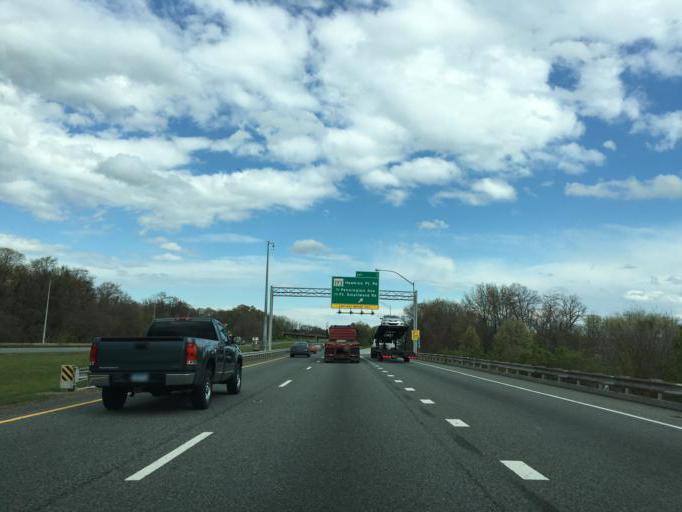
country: US
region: Maryland
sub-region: Anne Arundel County
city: Brooklyn Park
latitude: 39.2050
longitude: -76.5664
